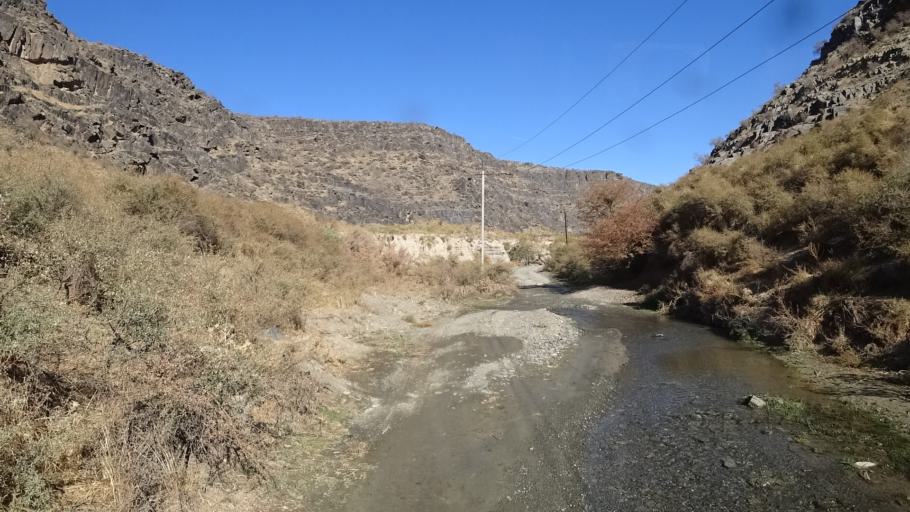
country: UZ
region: Navoiy
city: Nurota
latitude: 40.3078
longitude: 65.6198
